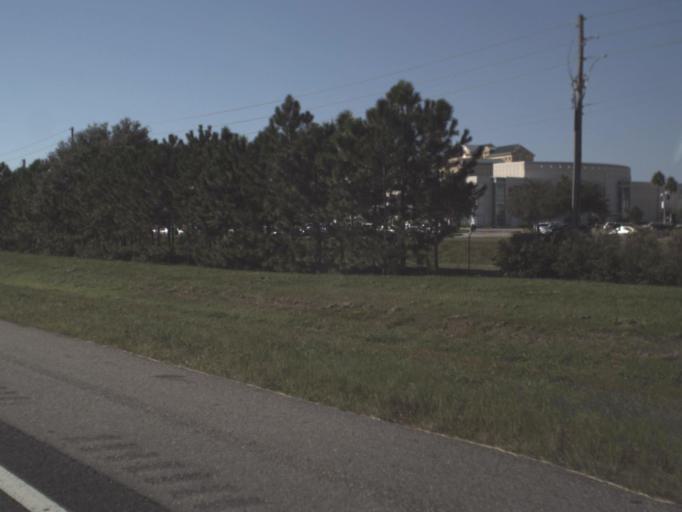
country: US
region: Florida
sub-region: Orange County
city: Sky Lake
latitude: 28.4427
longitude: -81.3906
